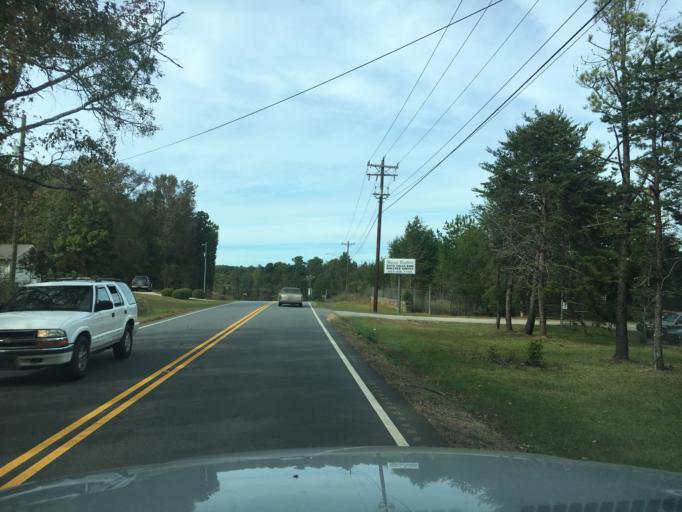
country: US
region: South Carolina
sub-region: Spartanburg County
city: Duncan
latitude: 34.8664
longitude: -82.1151
